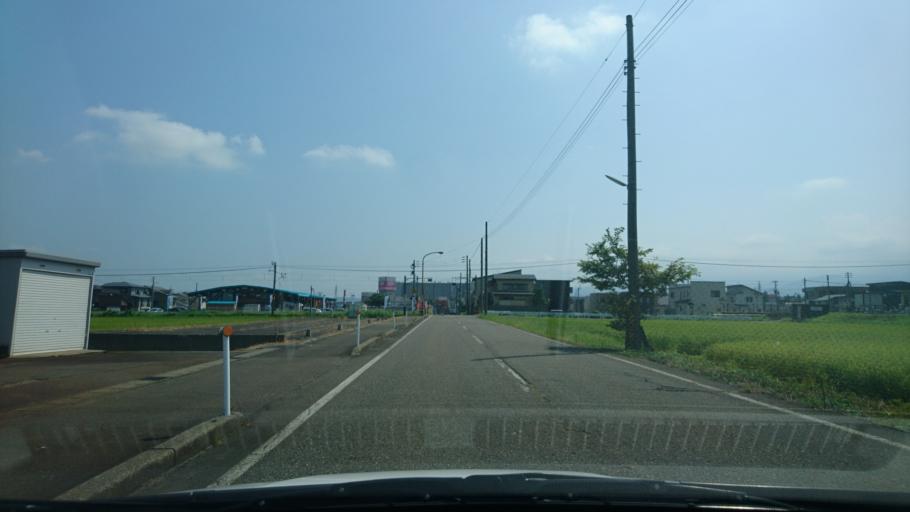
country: JP
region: Niigata
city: Arai
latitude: 37.0536
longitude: 138.2567
